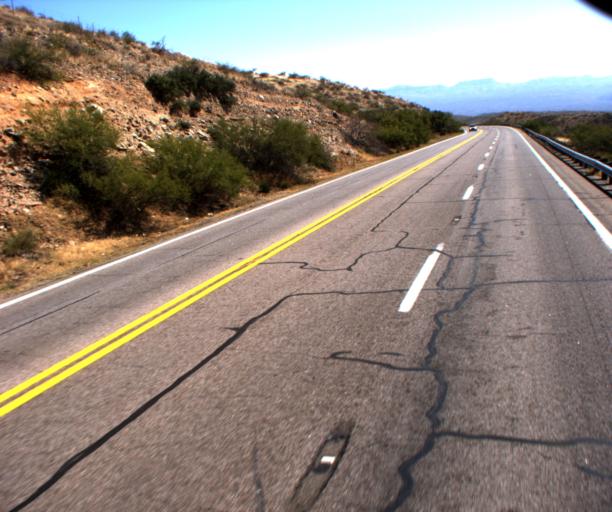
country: US
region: Arizona
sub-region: Pinal County
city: Oracle
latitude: 32.6383
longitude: -110.7261
